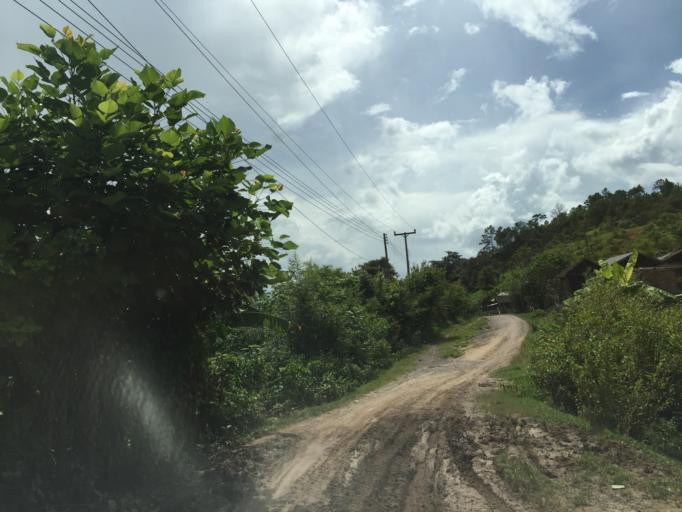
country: LA
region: Xiangkhoang
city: Muang Phonsavan
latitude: 19.3409
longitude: 103.5436
